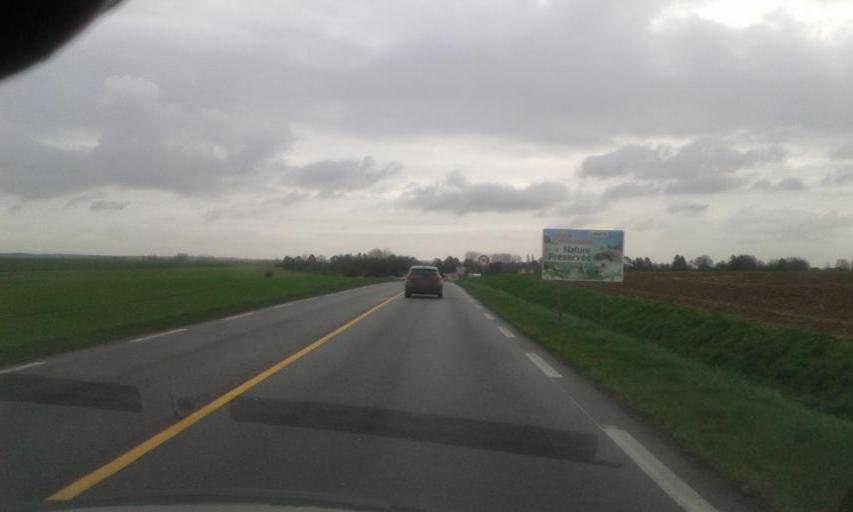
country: FR
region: Haute-Normandie
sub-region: Departement de l'Eure
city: Pont-Saint-Pierre
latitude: 49.3882
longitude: 1.2928
